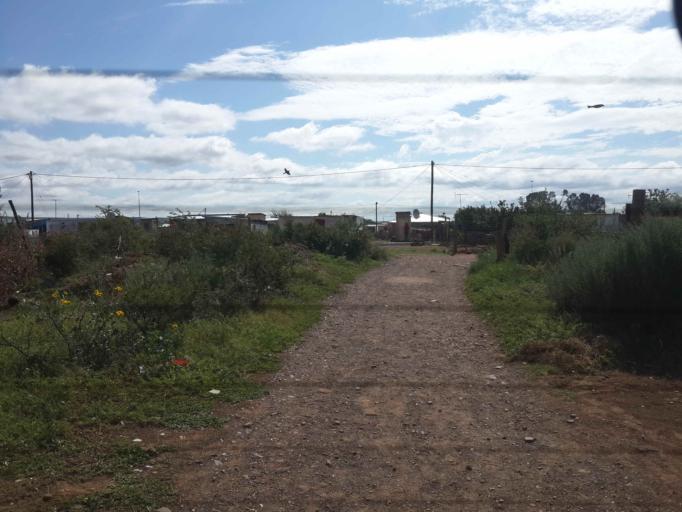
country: ZA
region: Northern Cape
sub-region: Siyanda District Municipality
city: Danielskuil
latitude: -28.1928
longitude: 23.5421
